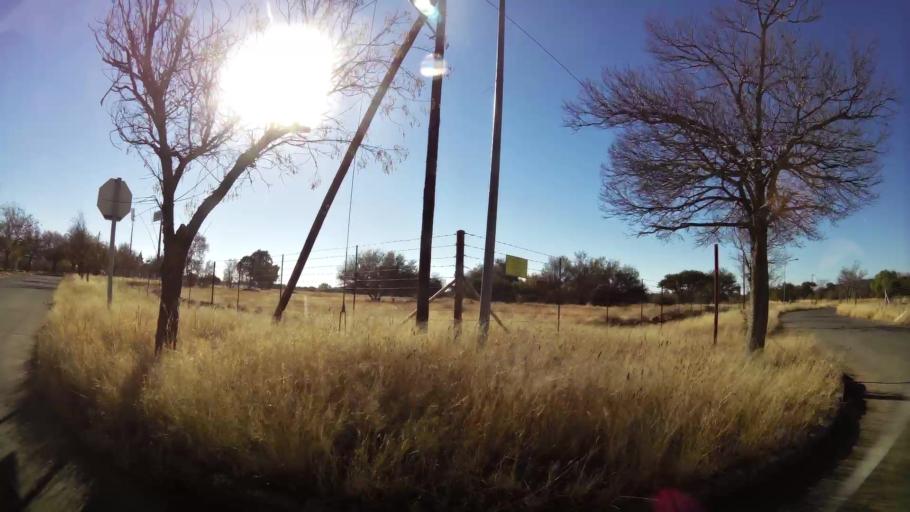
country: ZA
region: Northern Cape
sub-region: Frances Baard District Municipality
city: Kimberley
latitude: -28.7454
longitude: 24.7970
